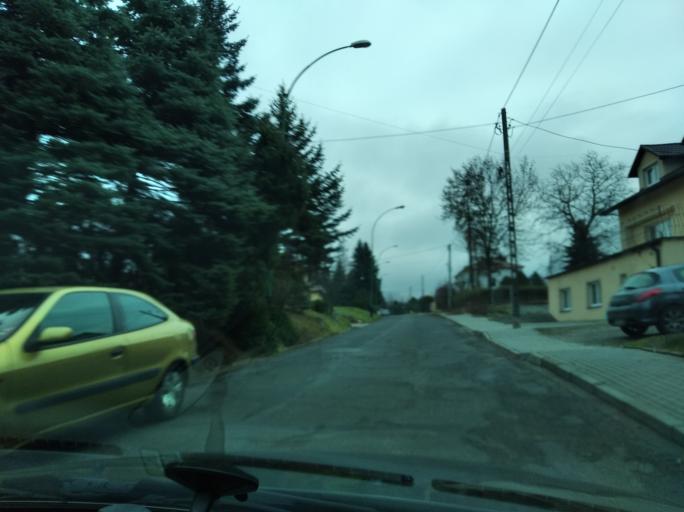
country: PL
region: Subcarpathian Voivodeship
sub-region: Powiat lancucki
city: Lancut
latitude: 50.0640
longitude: 22.2142
